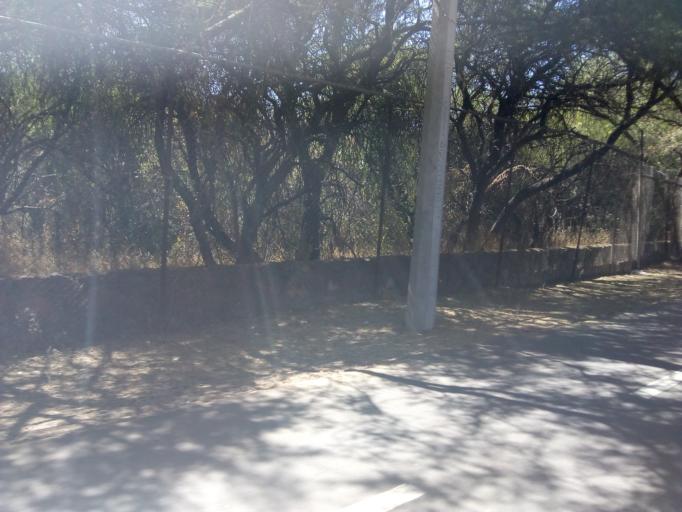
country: MX
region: Guanajuato
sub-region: Leon
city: La Ermita
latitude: 21.1772
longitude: -101.6985
